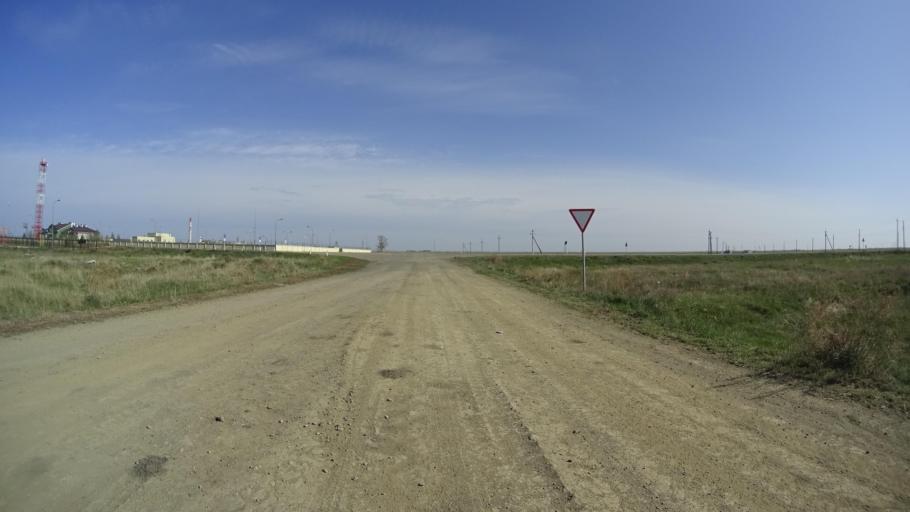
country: RU
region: Chelyabinsk
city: Chesma
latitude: 53.7914
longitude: 61.0435
